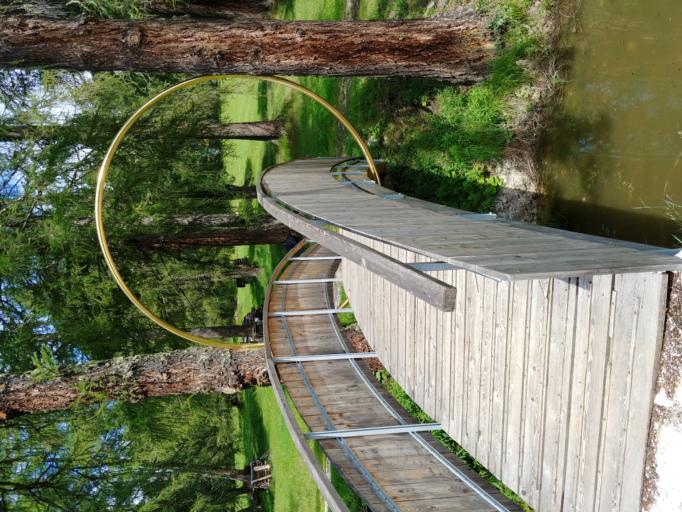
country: IT
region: Trentino-Alto Adige
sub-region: Bolzano
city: Santa Cristina Valgardena
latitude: 46.5498
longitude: 11.7099
